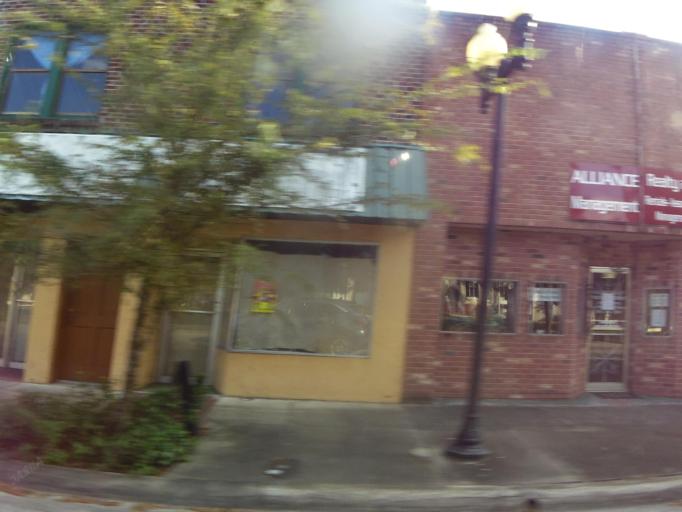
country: US
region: Florida
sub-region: Putnam County
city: Palatka
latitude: 29.6469
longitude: -81.6328
